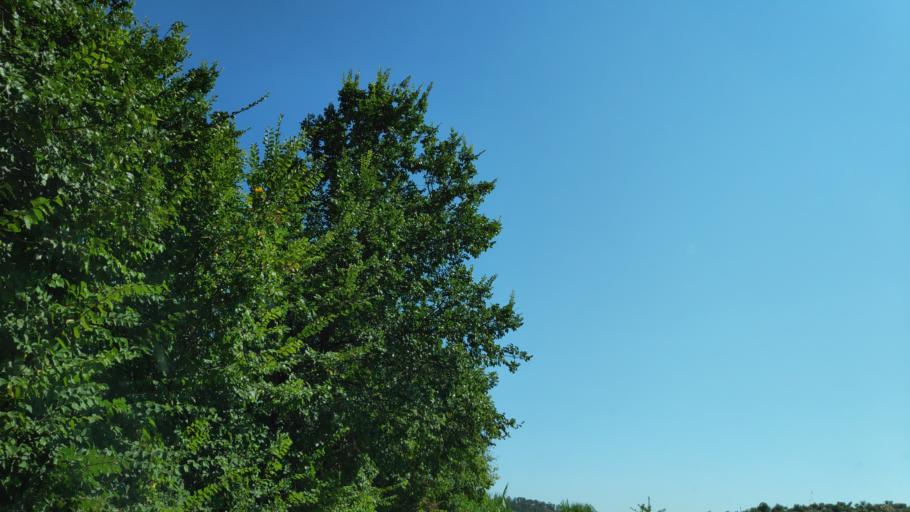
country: IT
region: Calabria
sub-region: Provincia di Reggio Calabria
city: Monasterace
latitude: 38.4345
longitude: 16.5252
